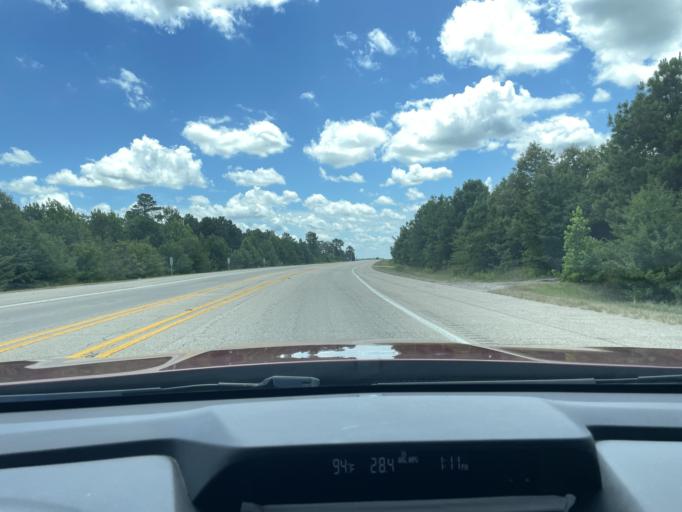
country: US
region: Arkansas
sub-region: Drew County
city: Monticello
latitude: 33.7093
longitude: -91.8081
